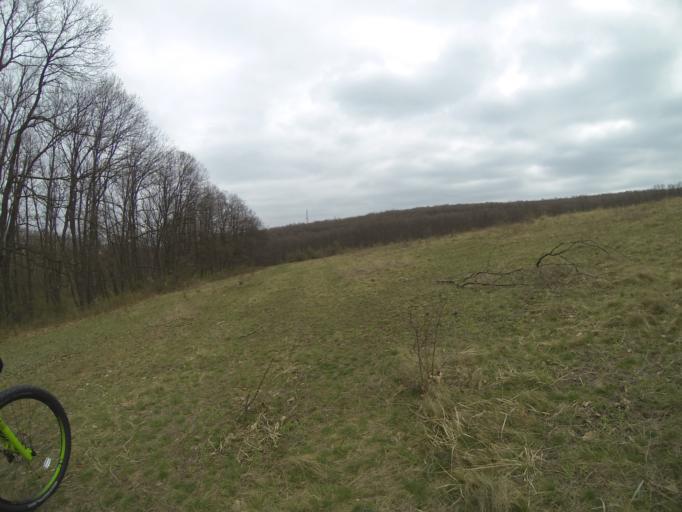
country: RO
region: Dolj
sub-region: Comuna Breasta
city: Breasta
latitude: 44.3172
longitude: 23.6474
